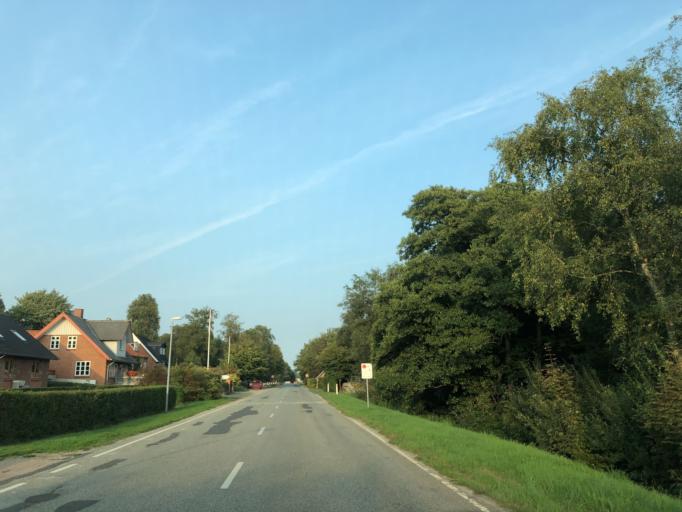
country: DK
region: South Denmark
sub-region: Vejle Kommune
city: Jelling
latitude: 55.7082
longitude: 9.4513
